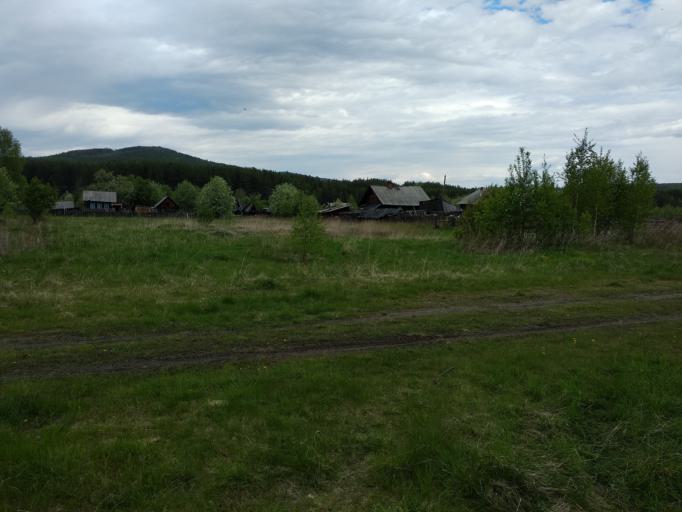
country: RU
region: Sverdlovsk
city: Karpinsk
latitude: 59.7143
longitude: 59.5982
